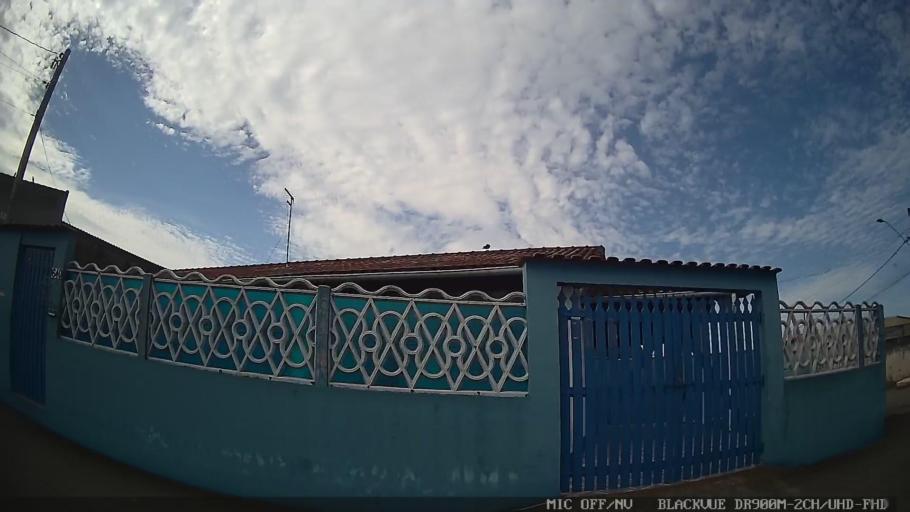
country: BR
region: Sao Paulo
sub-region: Itanhaem
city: Itanhaem
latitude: -24.1605
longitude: -46.7647
